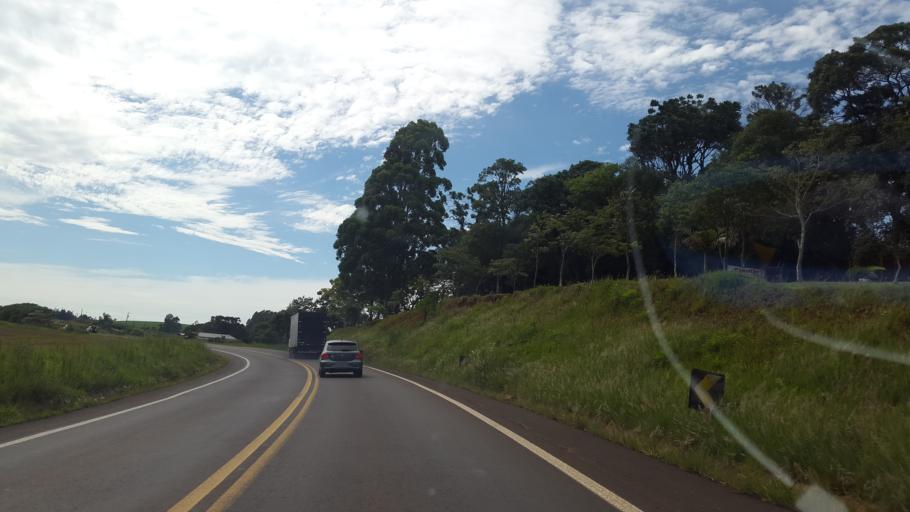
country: AR
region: Misiones
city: Bernardo de Irigoyen
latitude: -26.2682
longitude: -53.5937
